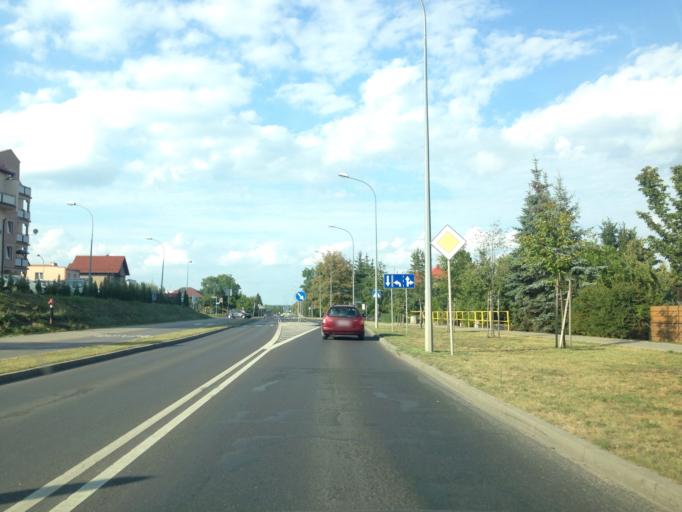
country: PL
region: Warmian-Masurian Voivodeship
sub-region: Powiat ilawski
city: Ilawa
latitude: 53.6063
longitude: 19.5683
